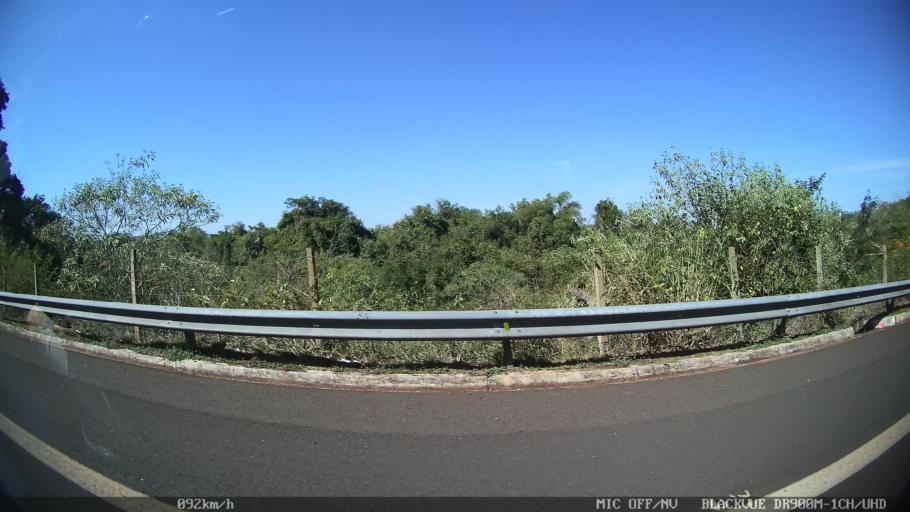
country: BR
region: Sao Paulo
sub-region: Batatais
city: Batatais
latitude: -20.7279
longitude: -47.5194
